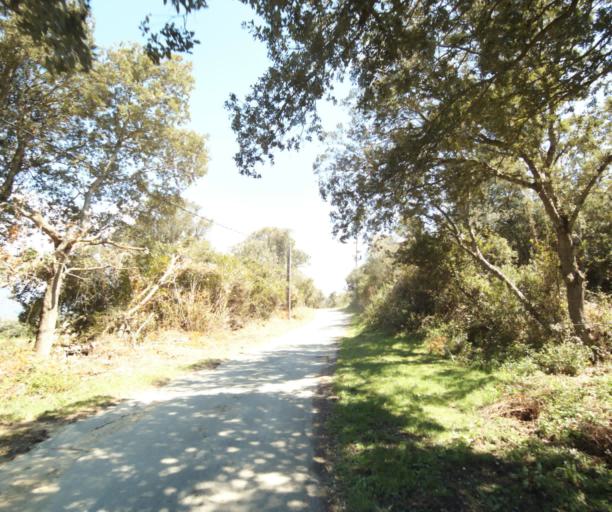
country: FR
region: Corsica
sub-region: Departement de la Corse-du-Sud
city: Propriano
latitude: 41.6412
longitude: 8.8692
